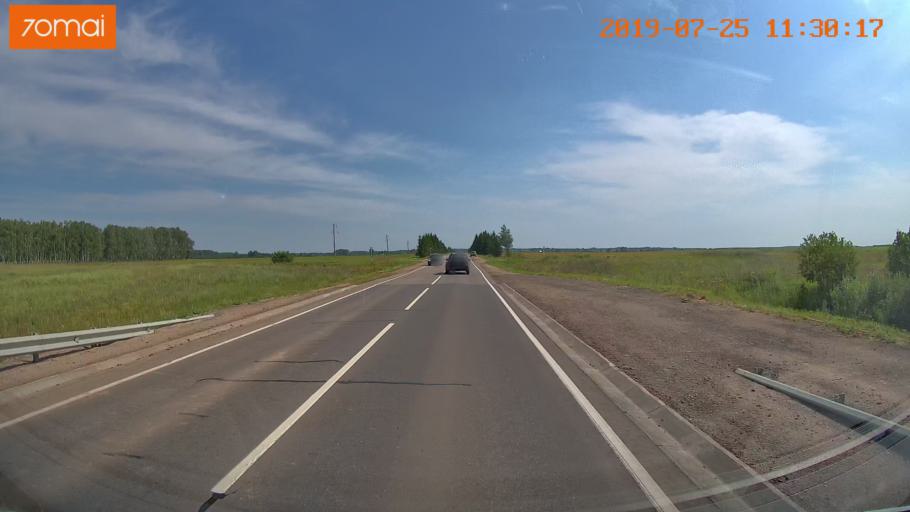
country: RU
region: Ivanovo
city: Privolzhsk
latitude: 57.3867
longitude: 41.3204
